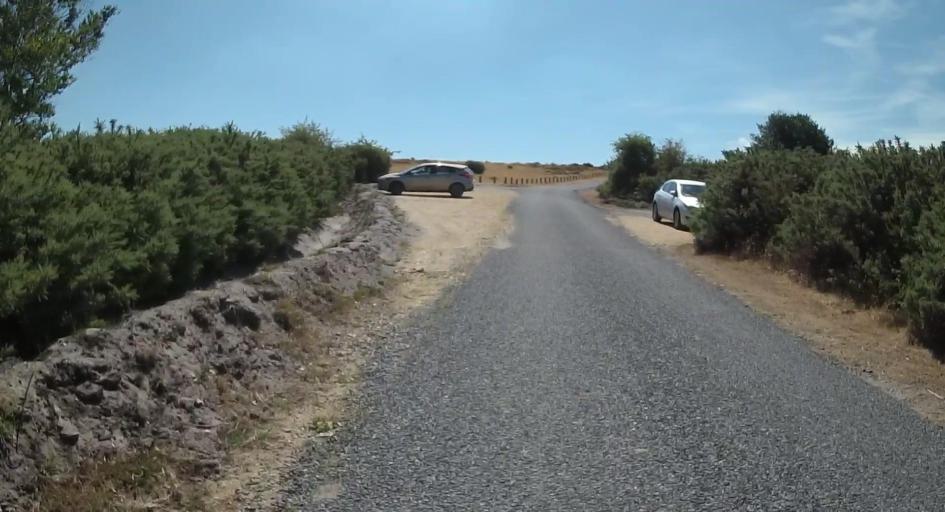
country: GB
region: England
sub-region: Dorset
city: Wareham
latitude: 50.6678
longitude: -2.0532
